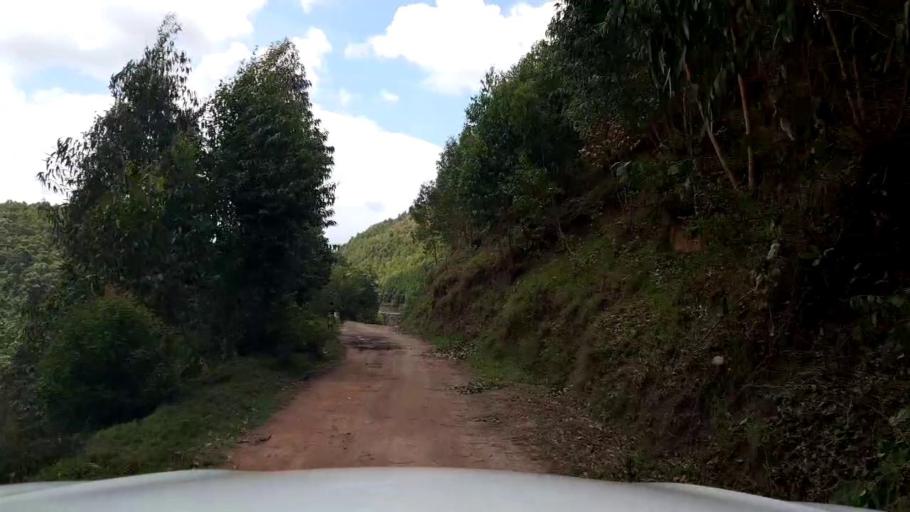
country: RW
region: Northern Province
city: Byumba
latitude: -1.5249
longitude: 30.1307
